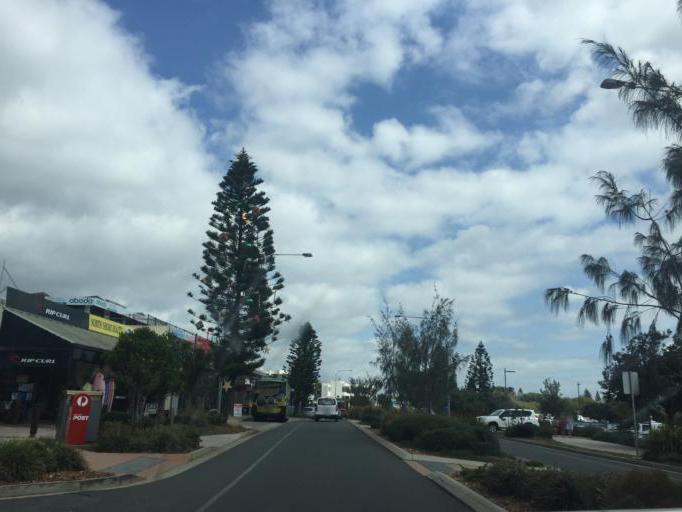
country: AU
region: Queensland
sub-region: Sunshine Coast
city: Coolum Beach
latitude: -26.5305
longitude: 153.0915
